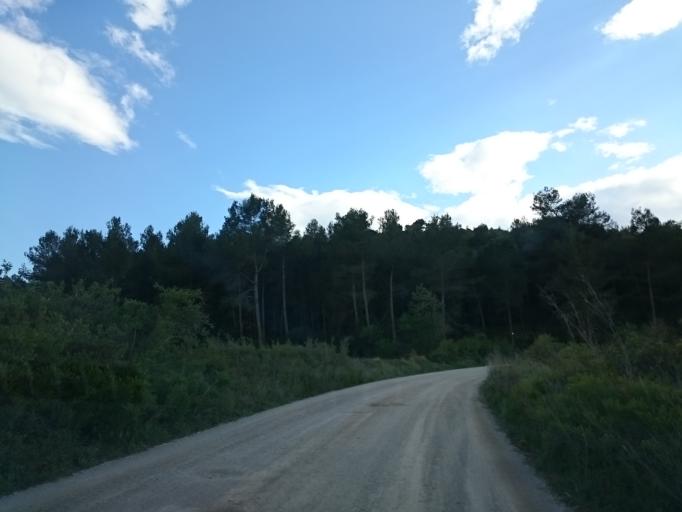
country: ES
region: Catalonia
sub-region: Provincia de Barcelona
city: Begues
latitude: 41.3239
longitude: 1.9248
